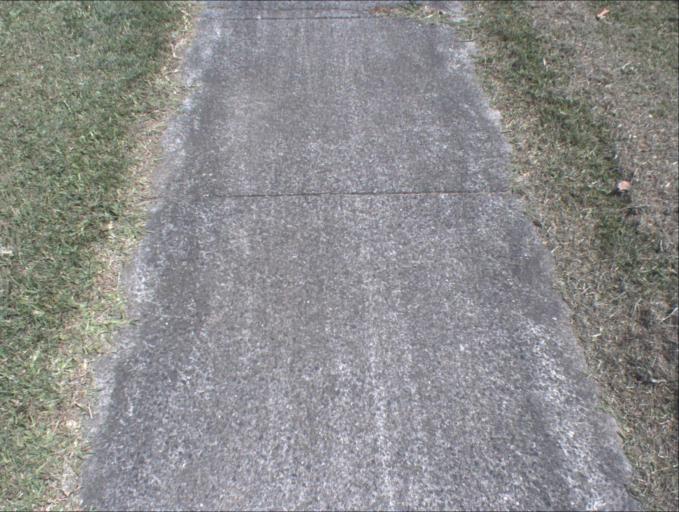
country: AU
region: Queensland
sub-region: Logan
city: Slacks Creek
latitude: -27.6408
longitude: 153.1506
